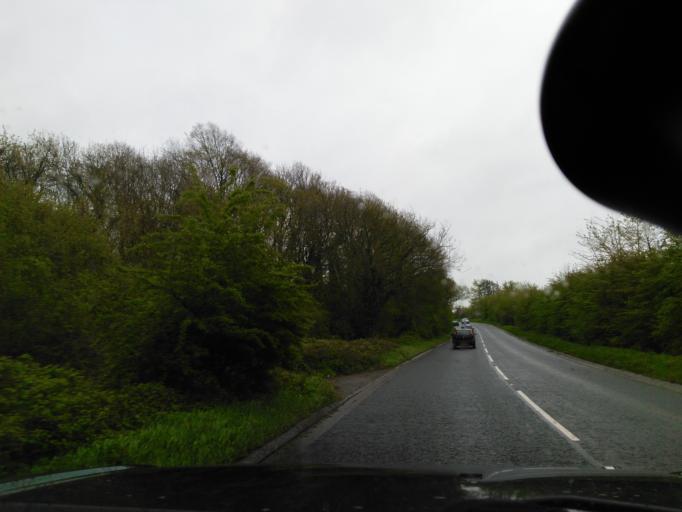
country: GB
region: England
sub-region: Wiltshire
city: Bradford-on-Avon
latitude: 51.3706
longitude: -2.2717
